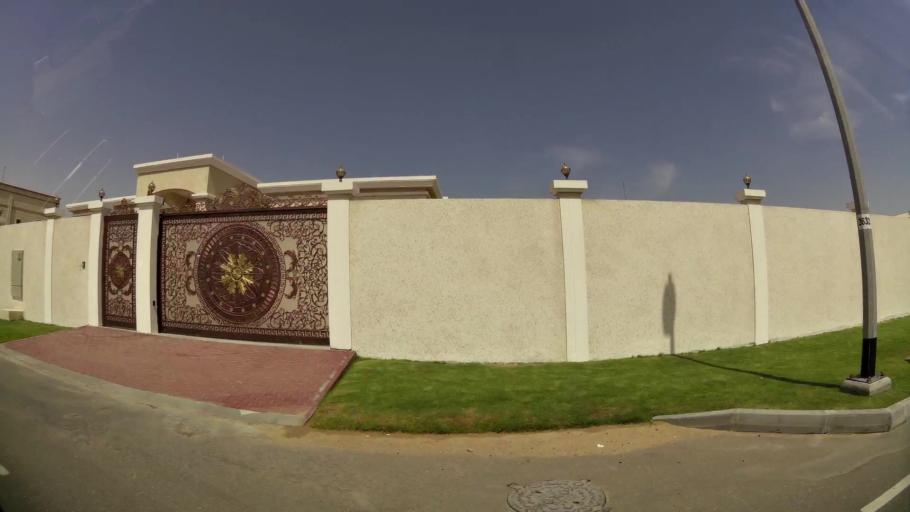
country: AE
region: Ash Shariqah
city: Sharjah
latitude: 25.1874
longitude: 55.4371
